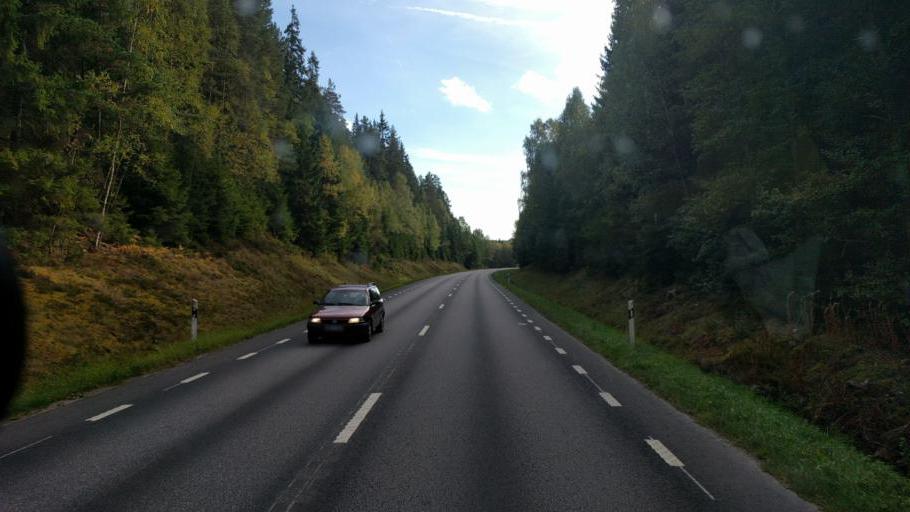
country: SE
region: OEstergoetland
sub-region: Kinda Kommun
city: Kisa
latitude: 57.9523
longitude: 15.6628
